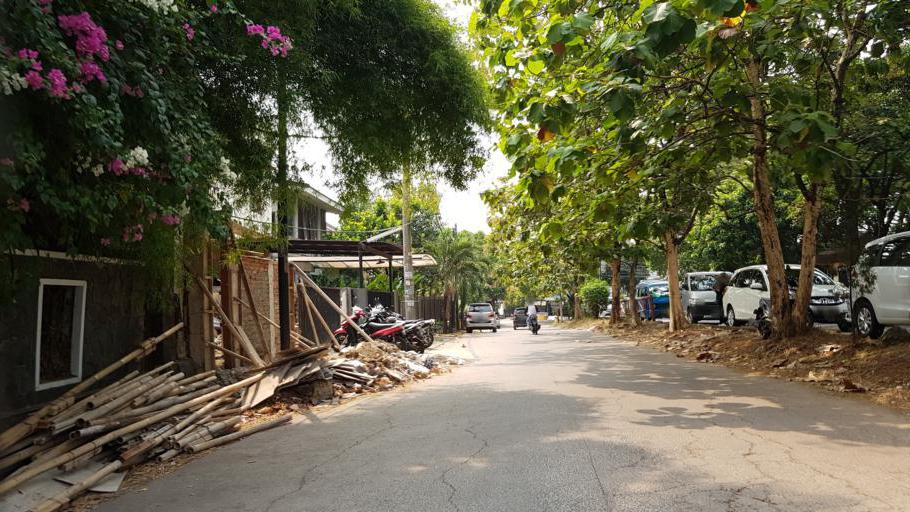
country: ID
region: West Java
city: Pamulang
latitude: -6.3270
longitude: 106.7864
